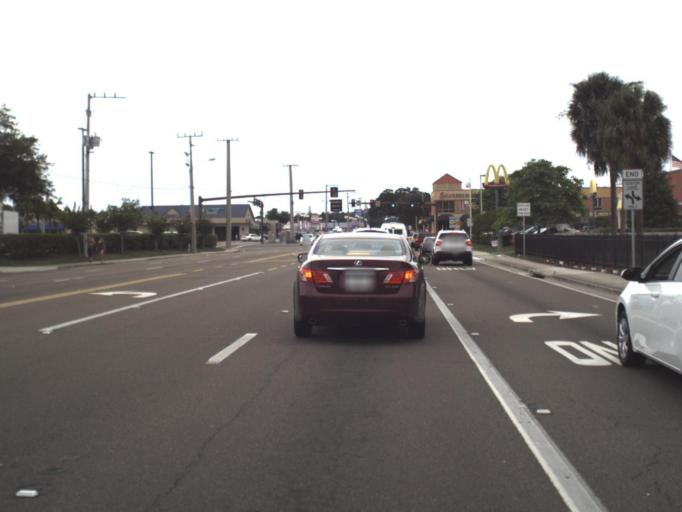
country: US
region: Florida
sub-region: Sarasota County
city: South Sarasota
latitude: 27.2989
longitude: -82.5291
